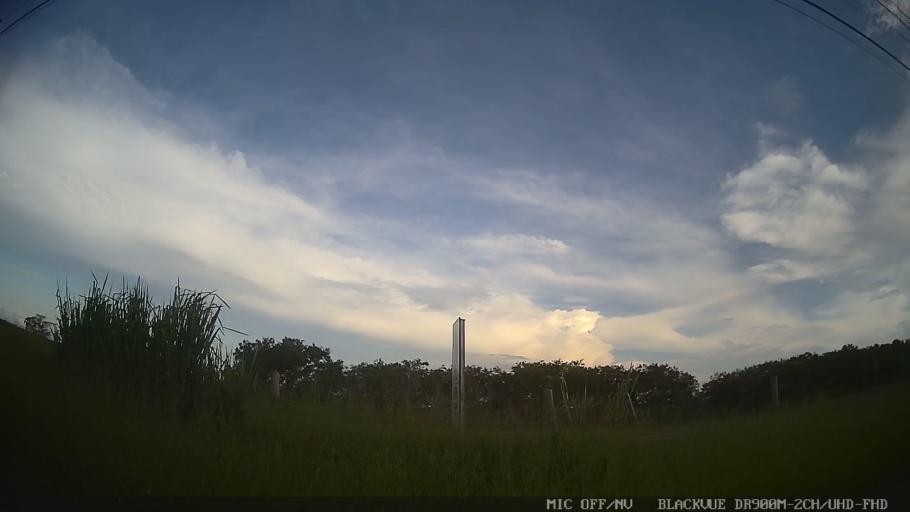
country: BR
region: Sao Paulo
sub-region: Tiete
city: Tiete
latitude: -23.0636
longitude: -47.7280
